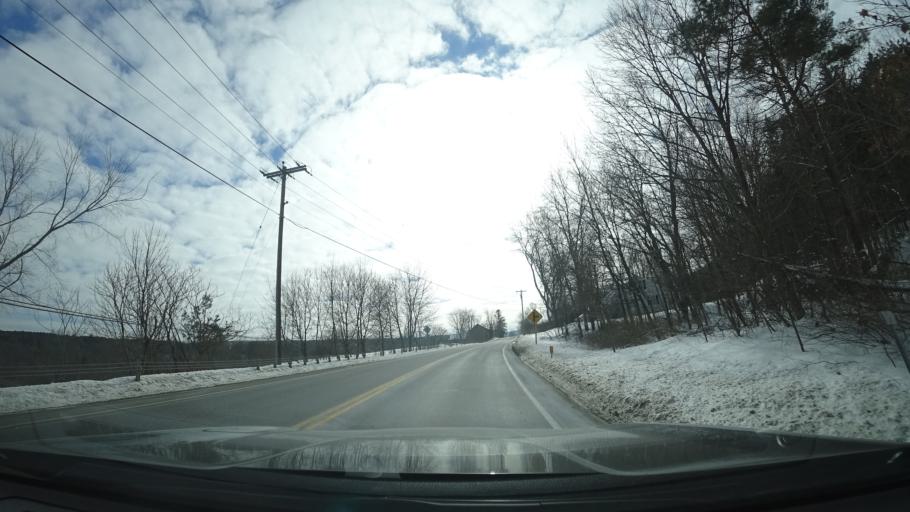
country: US
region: New York
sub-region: Washington County
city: Fort Edward
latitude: 43.2595
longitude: -73.5118
